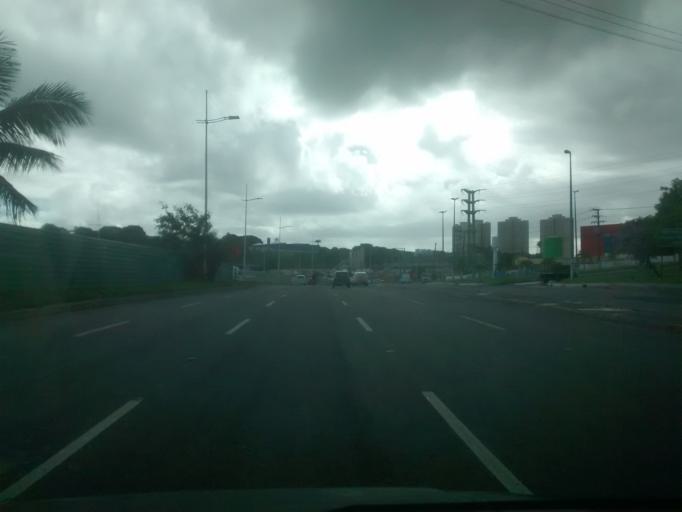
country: BR
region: Bahia
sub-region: Salvador
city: Salvador
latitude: -12.9430
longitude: -38.4192
